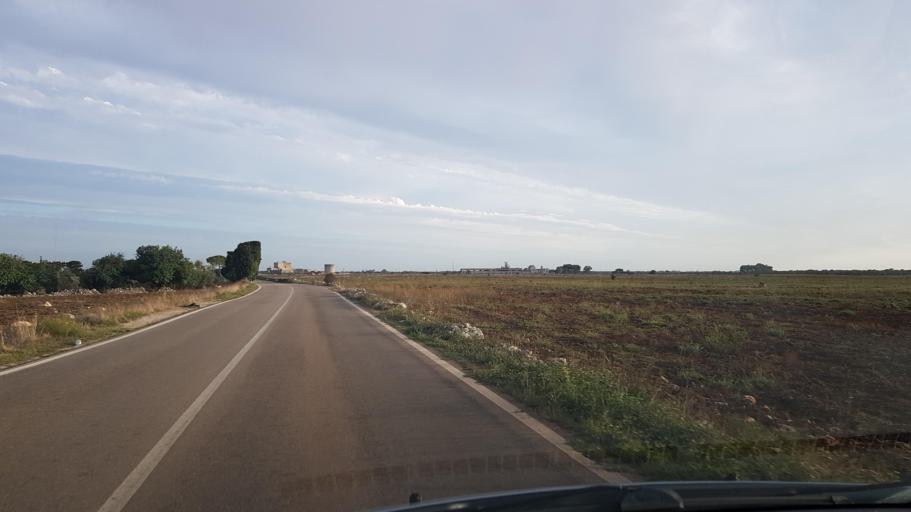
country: IT
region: Apulia
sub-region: Provincia di Lecce
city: Trepuzzi
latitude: 40.4431
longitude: 18.1098
